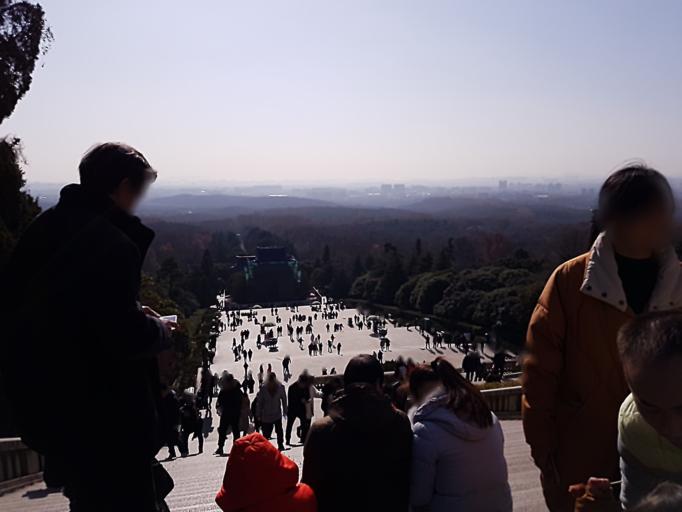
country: CN
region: Jiangsu Sheng
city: Xiaolingwei
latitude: 32.0642
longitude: 118.8485
